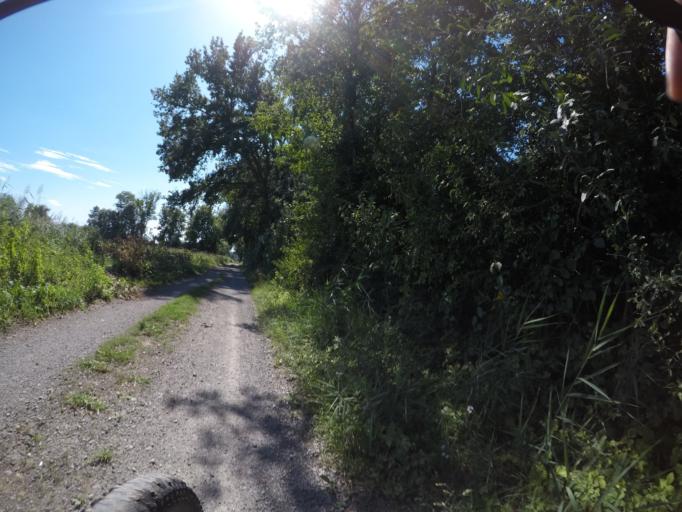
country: AT
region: Lower Austria
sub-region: Politischer Bezirk Wien-Umgebung
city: Moosbrunn
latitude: 48.0089
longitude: 16.4446
